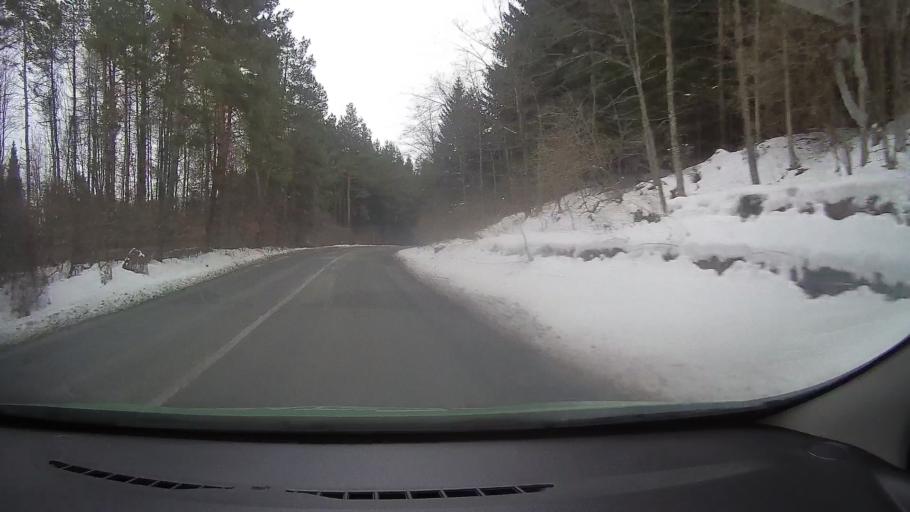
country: RO
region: Brasov
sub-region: Oras Predeal
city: Predeal
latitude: 45.5200
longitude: 25.5017
